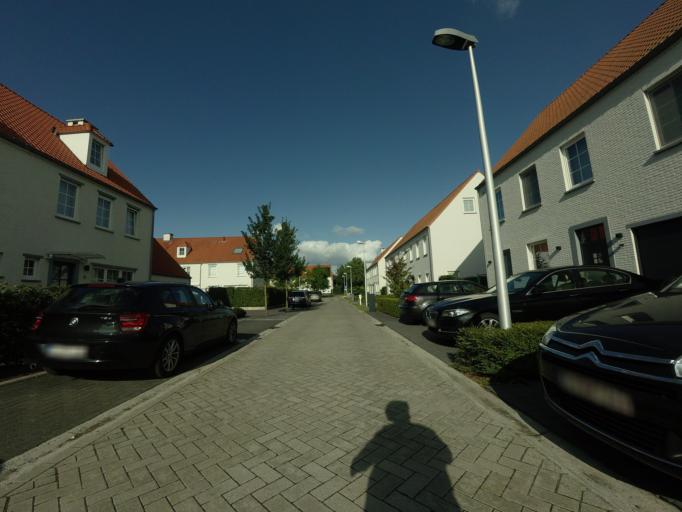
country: BE
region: Flanders
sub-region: Provincie Antwerpen
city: Edegem
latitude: 51.1546
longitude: 4.4247
